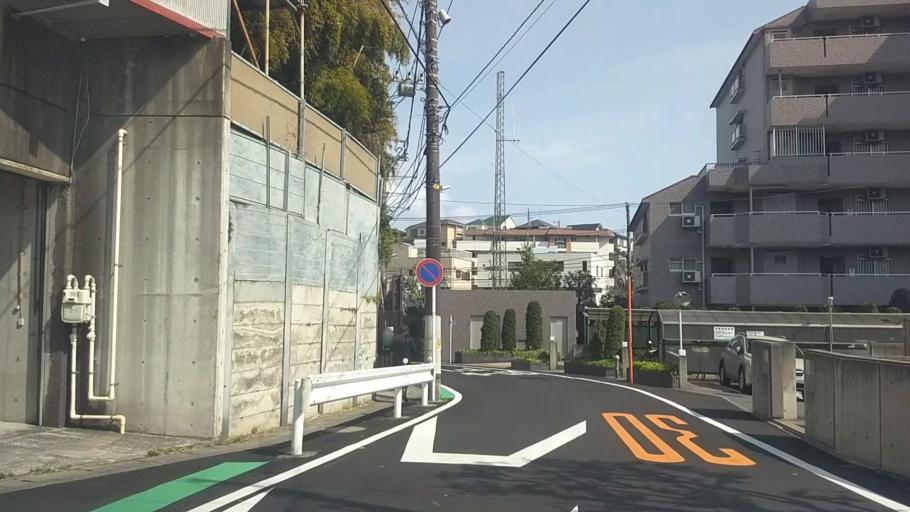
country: JP
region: Kanagawa
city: Kamakura
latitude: 35.3805
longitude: 139.5703
